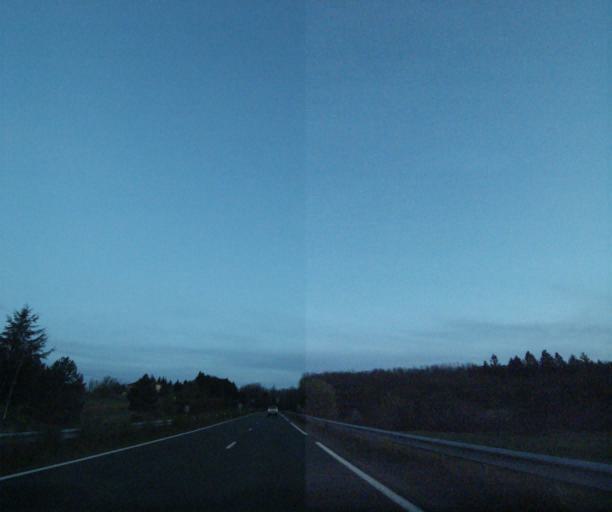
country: FR
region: Midi-Pyrenees
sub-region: Departement du Lot
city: Pradines
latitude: 44.5106
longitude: 1.4445
